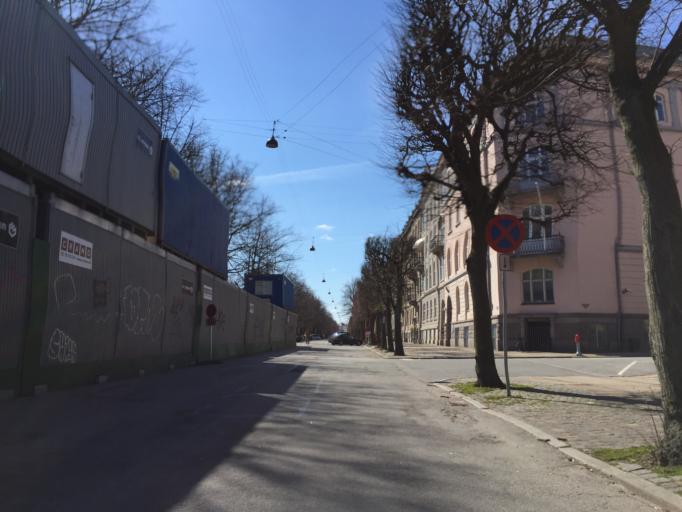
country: DK
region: Capital Region
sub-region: Kobenhavn
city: Christianshavn
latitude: 55.6928
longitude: 12.5841
